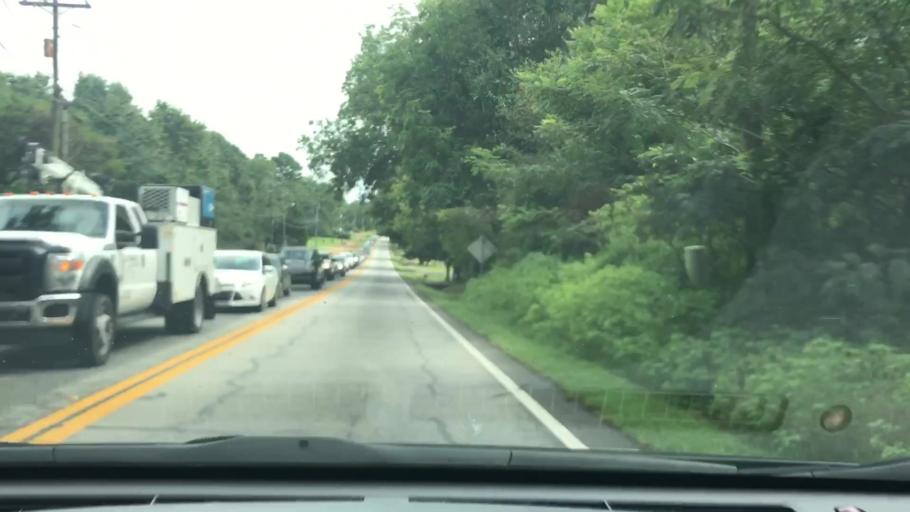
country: US
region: Georgia
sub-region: Walton County
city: Walnut Grove
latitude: 33.7405
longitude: -83.8524
